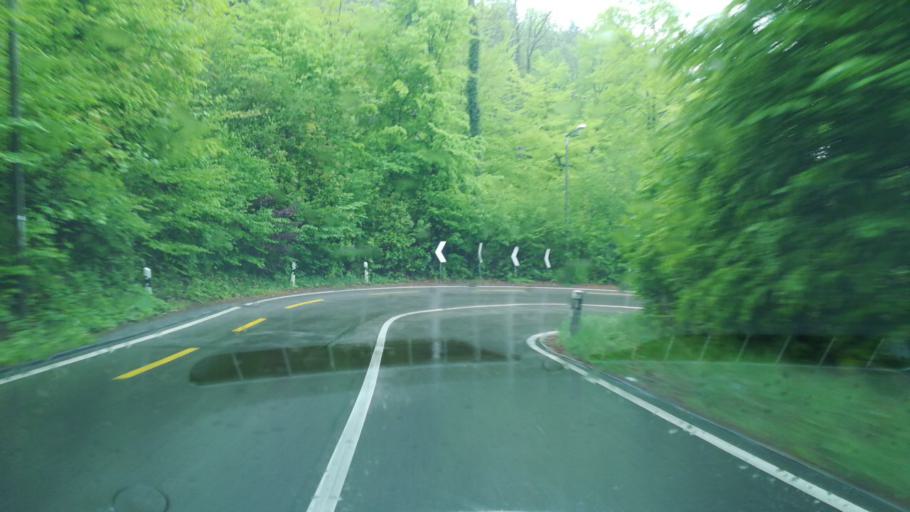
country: CH
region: Zurich
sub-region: Bezirk Winterthur
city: Toss
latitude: 47.4739
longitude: 8.6998
